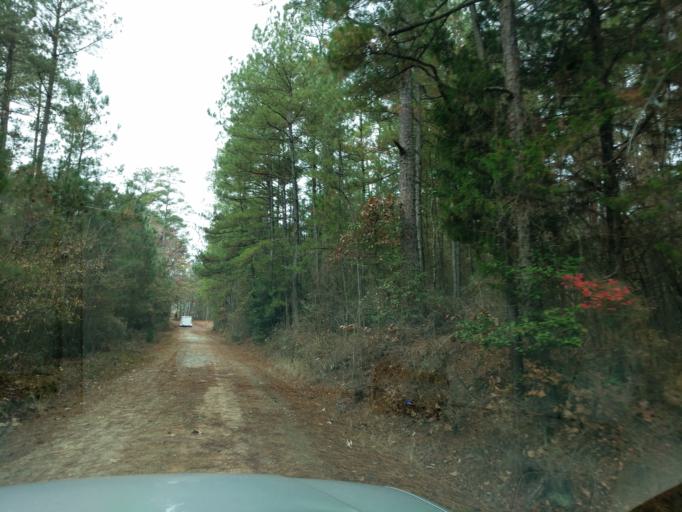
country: US
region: South Carolina
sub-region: Anderson County
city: Pendleton
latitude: 34.6526
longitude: -82.8109
